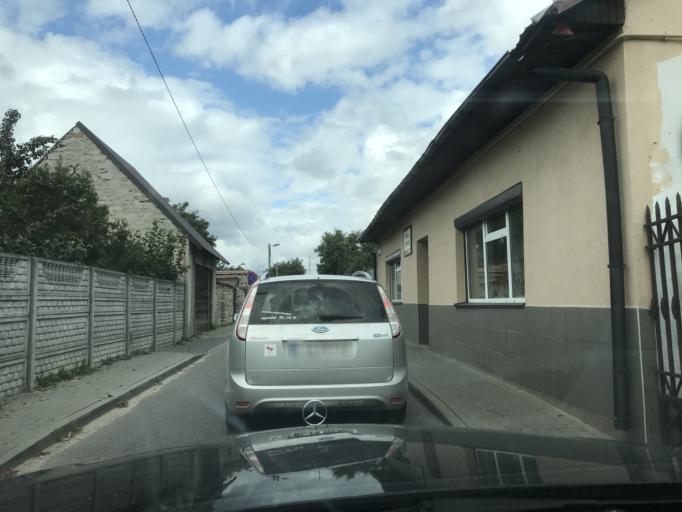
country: PL
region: Lublin Voivodeship
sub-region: Powiat janowski
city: Janow Lubelski
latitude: 50.7056
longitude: 22.4151
